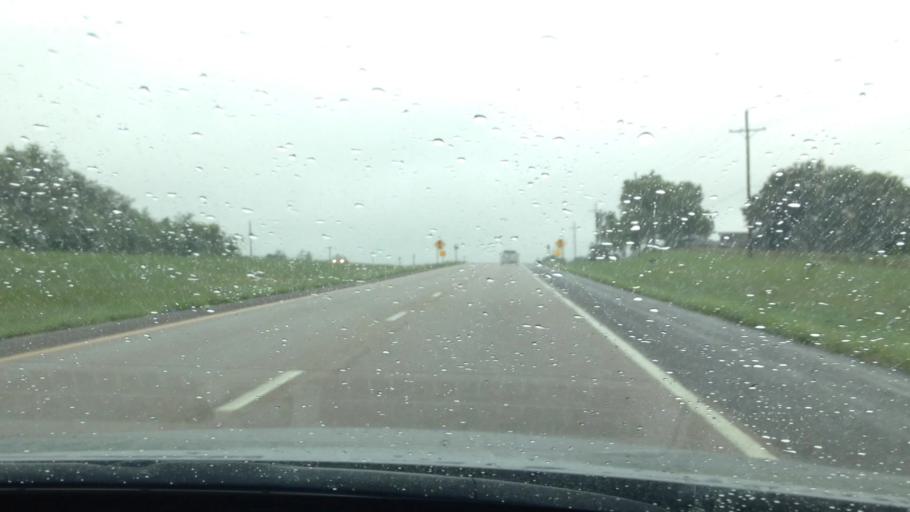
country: US
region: Kansas
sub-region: Leavenworth County
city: Lansing
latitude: 39.1967
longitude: -94.9010
